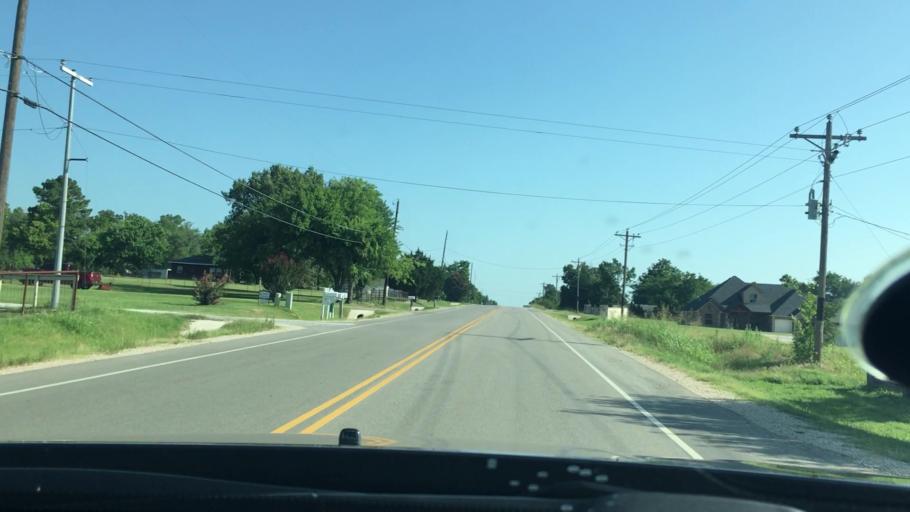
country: US
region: Oklahoma
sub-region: Pontotoc County
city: Ada
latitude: 34.8080
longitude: -96.6523
